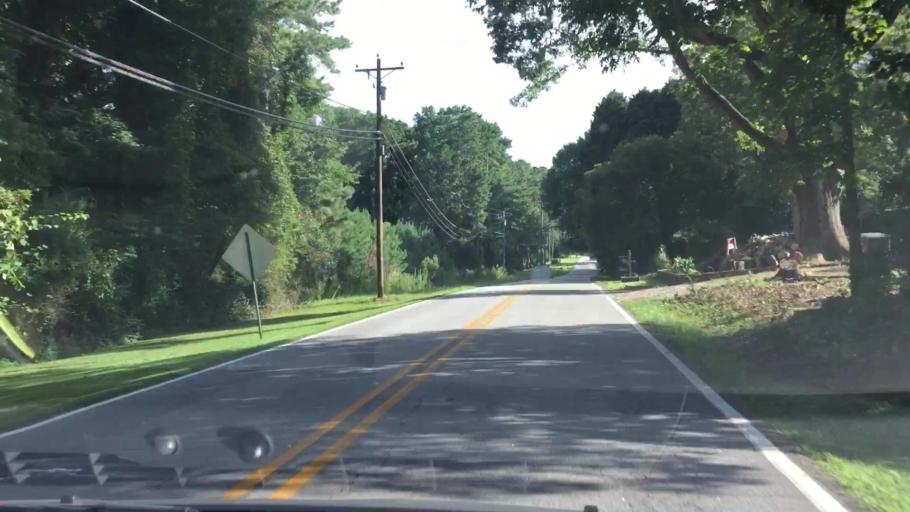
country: US
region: Georgia
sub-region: Henry County
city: Stockbridge
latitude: 33.6043
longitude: -84.1880
